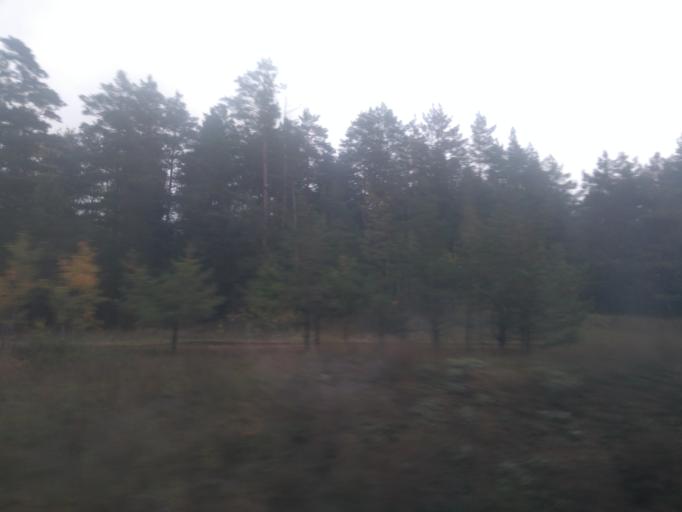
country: RU
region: Tatarstan
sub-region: Tukayevskiy Rayon
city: Naberezhnyye Chelny
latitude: 55.7274
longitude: 52.2570
